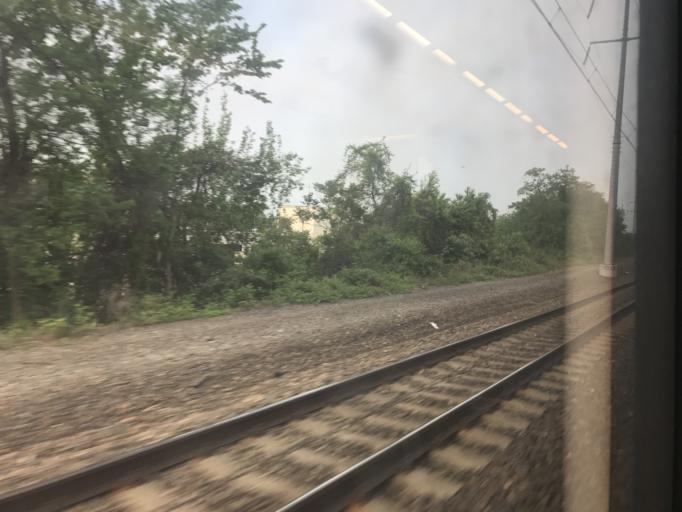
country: US
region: Maryland
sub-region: Prince George's County
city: Mount Rainier
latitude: 38.9183
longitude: -76.9765
